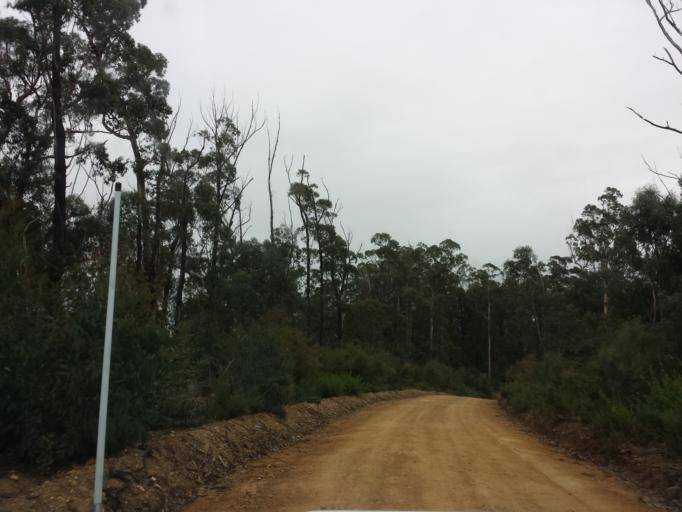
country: AU
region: Victoria
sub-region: Latrobe
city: Traralgon
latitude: -37.9839
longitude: 146.4403
